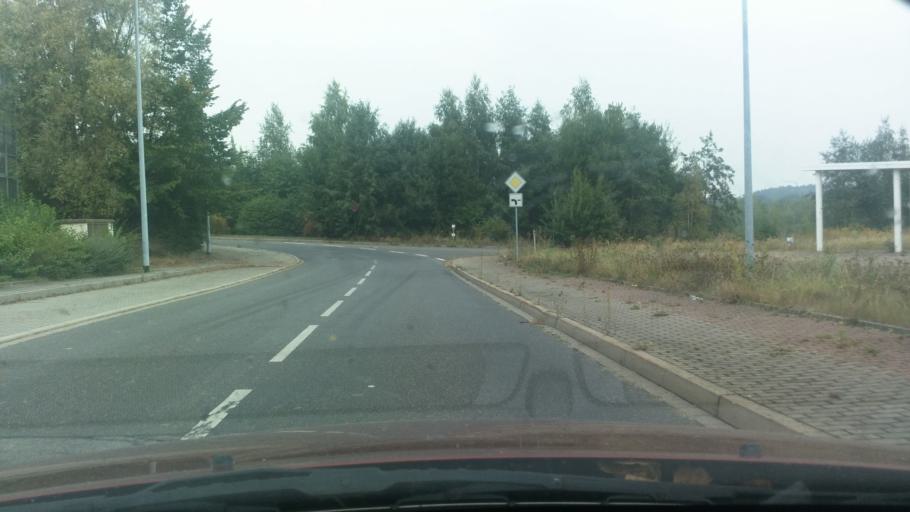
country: DE
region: Saxony
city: Goerlitz
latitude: 51.1882
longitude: 14.9603
